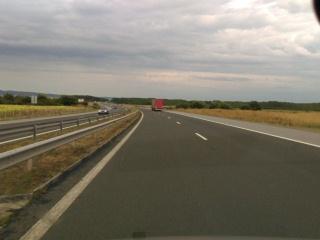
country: BG
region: Yambol
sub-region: Obshtina Yambol
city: Yambol
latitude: 42.5417
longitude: 26.4868
